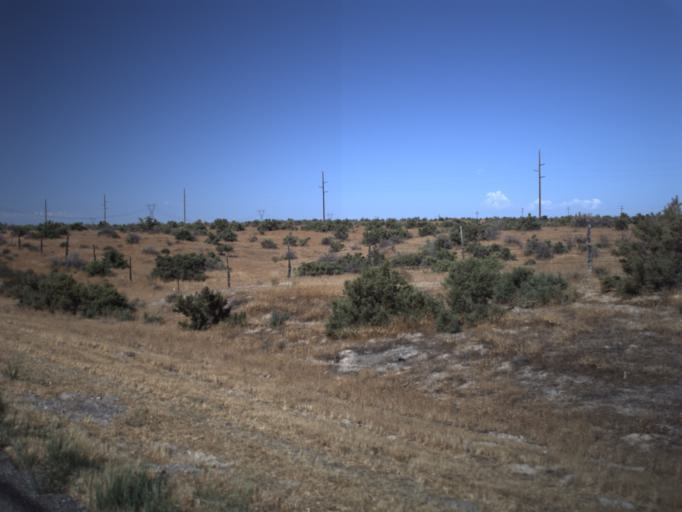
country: US
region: Utah
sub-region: Millard County
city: Delta
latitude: 39.4982
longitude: -112.3945
